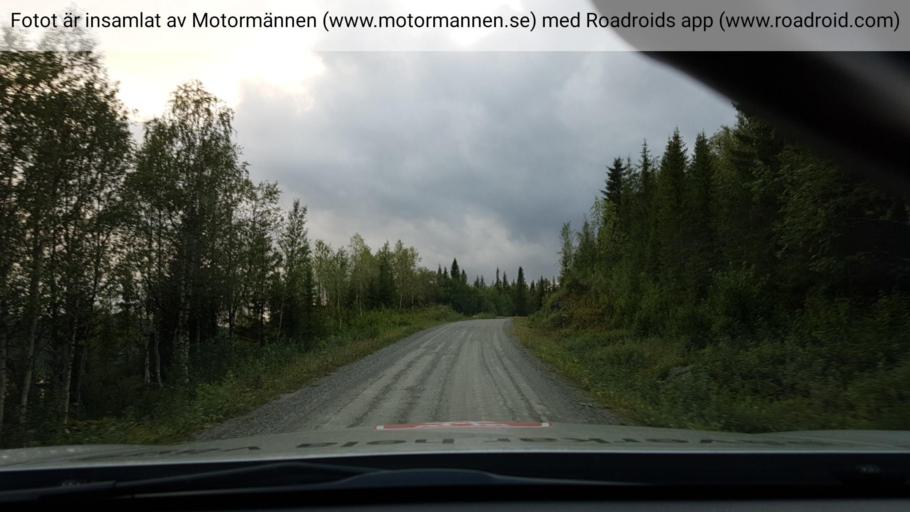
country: SE
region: Vaesterbotten
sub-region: Vilhelmina Kommun
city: Sjoberg
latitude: 65.4930
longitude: 15.5007
